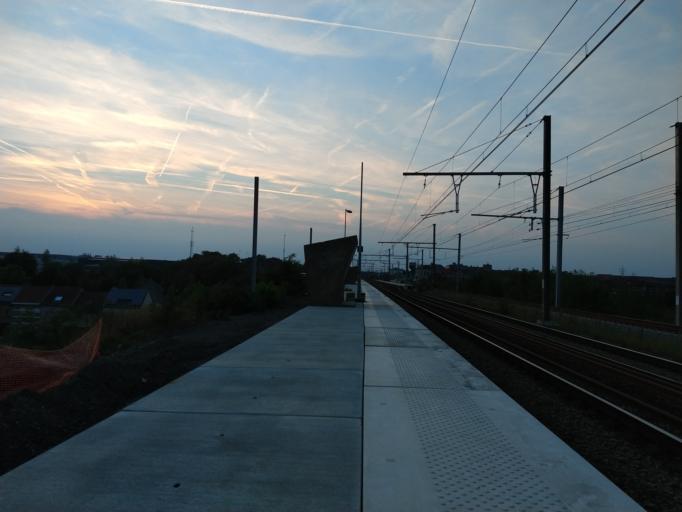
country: BE
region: Flanders
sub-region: Provincie Vlaams-Brabant
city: Tienen
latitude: 50.8047
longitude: 4.9301
